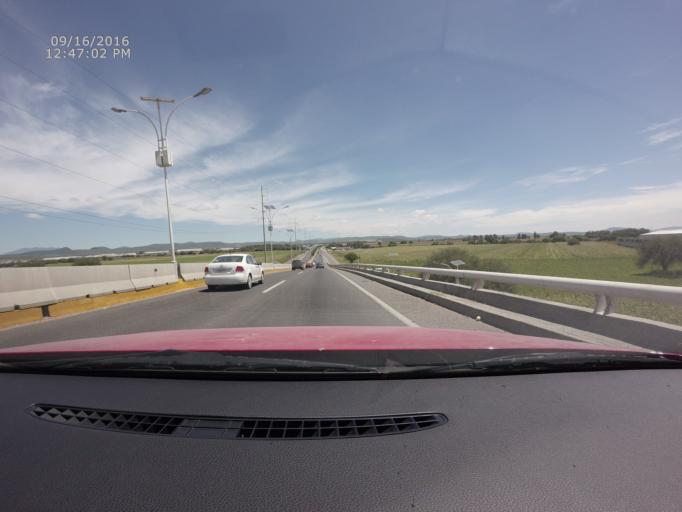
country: MX
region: Queretaro
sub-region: Colon
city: Purisima de Cubos (La Purisima)
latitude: 20.5970
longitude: -100.1774
